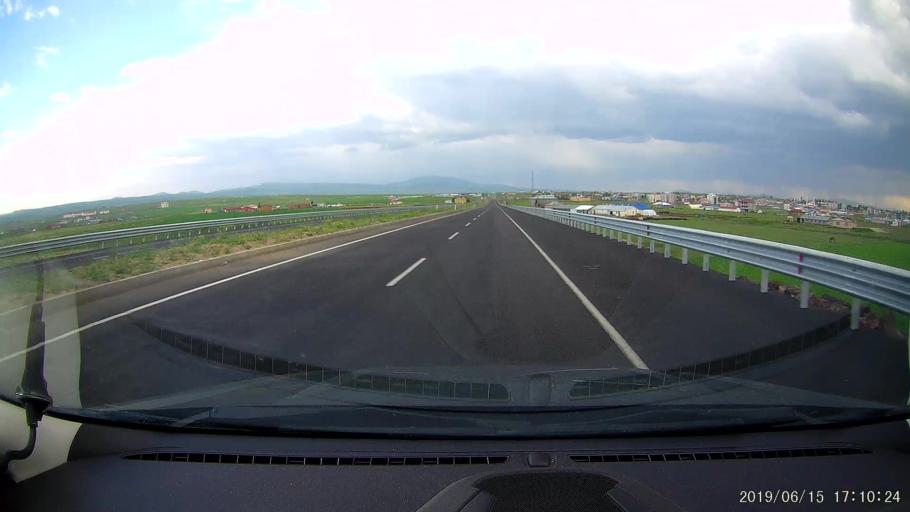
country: TR
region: Kars
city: Kars
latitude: 40.6225
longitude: 43.1337
